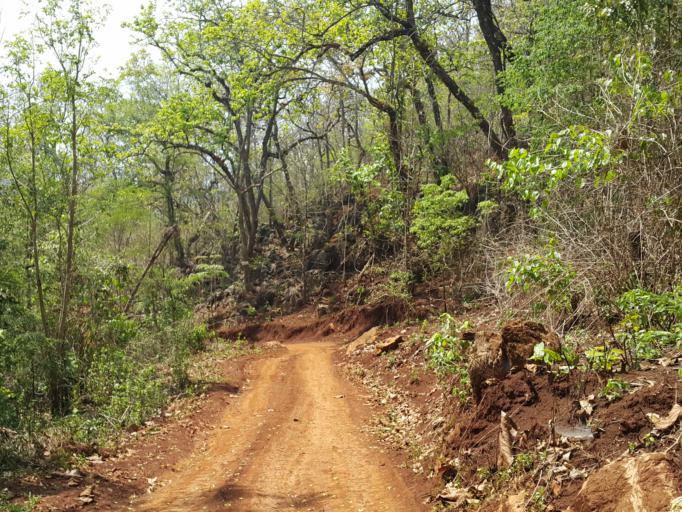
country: TH
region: Chiang Mai
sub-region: Amphoe Chiang Dao
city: Chiang Dao
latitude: 19.3066
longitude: 98.7257
